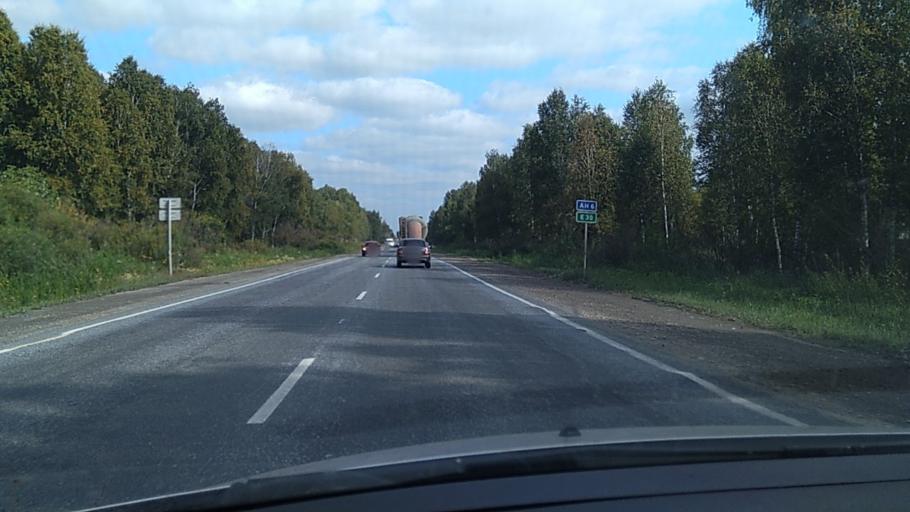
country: RU
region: Chelyabinsk
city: Chebarkul'
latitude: 54.9222
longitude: 60.2940
